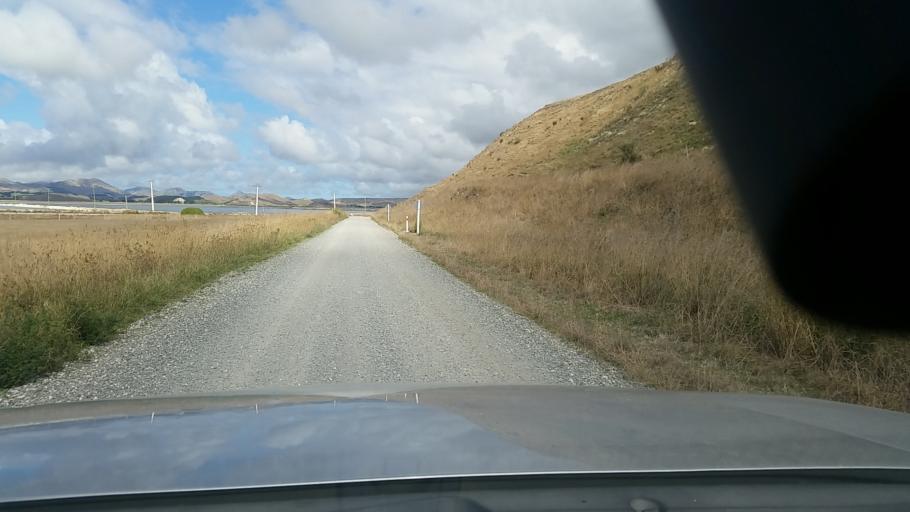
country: NZ
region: Marlborough
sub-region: Marlborough District
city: Blenheim
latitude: -41.7030
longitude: 174.1501
